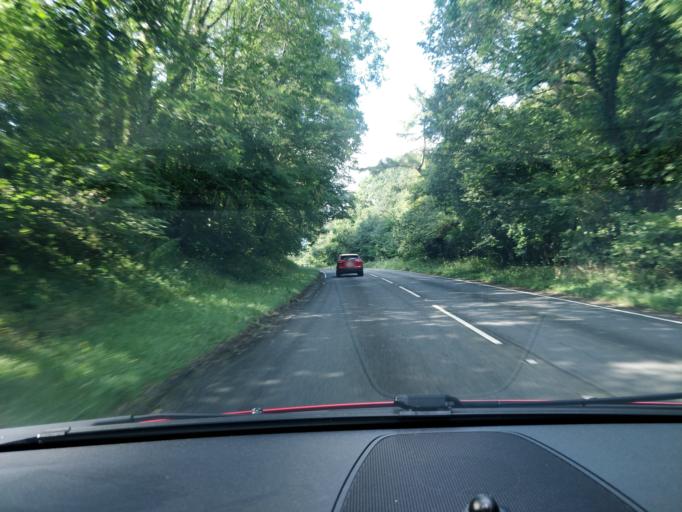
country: GB
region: Wales
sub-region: Conwy
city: Llansantffraid Glan Conwy
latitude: 53.2208
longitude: -3.8226
